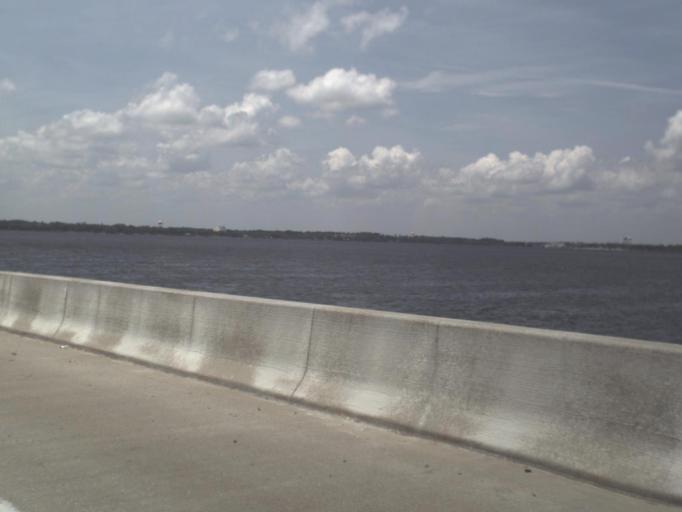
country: US
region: Florida
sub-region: Clay County
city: Orange Park
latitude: 30.1894
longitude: -81.6513
